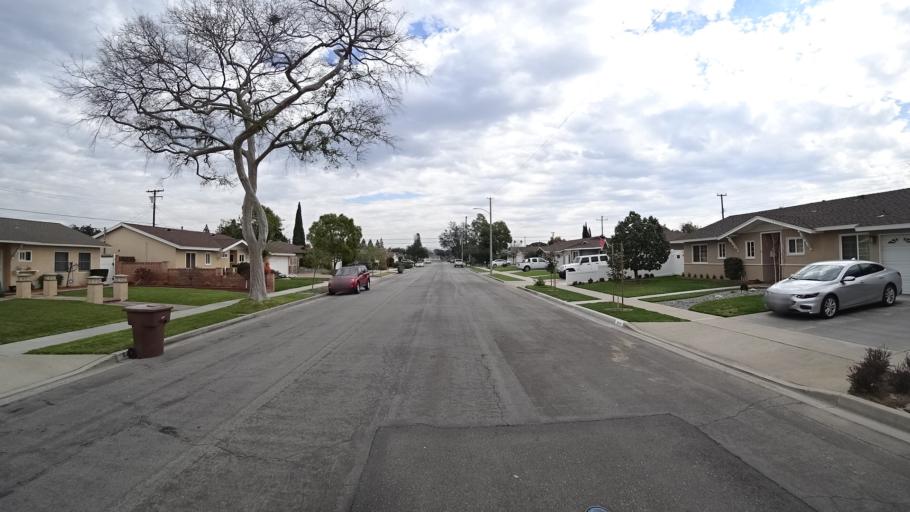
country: US
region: California
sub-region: Orange County
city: Anaheim
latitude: 33.8341
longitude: -117.8859
